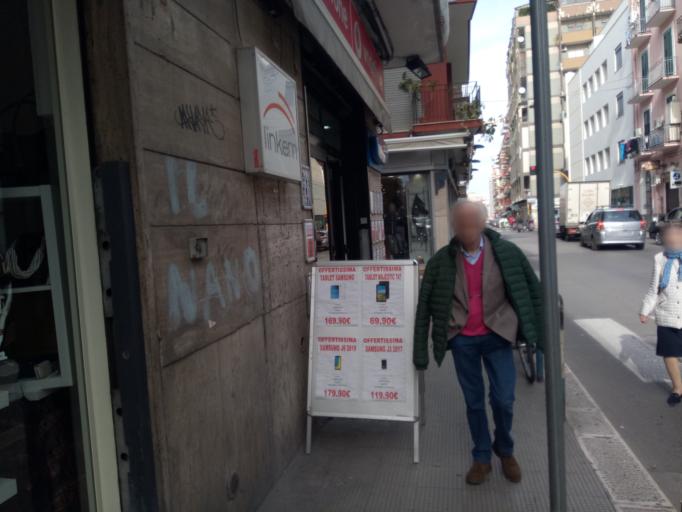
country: IT
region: Apulia
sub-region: Provincia di Bari
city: Bari
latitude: 41.1097
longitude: 16.8678
